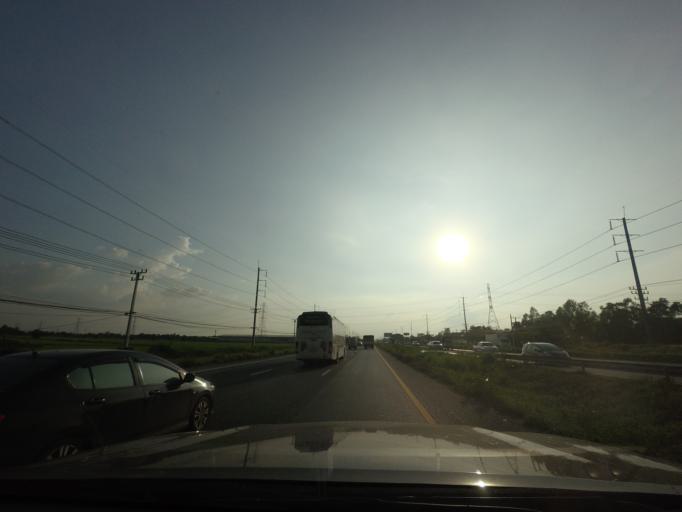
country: TH
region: Sara Buri
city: Nong Khae
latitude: 14.2757
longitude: 100.8054
